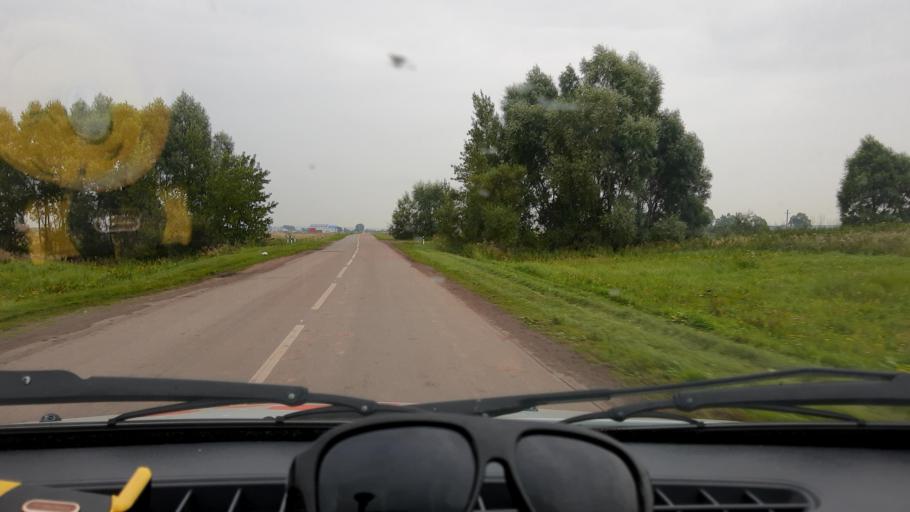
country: RU
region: Bashkortostan
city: Blagoveshchensk
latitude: 55.0036
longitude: 55.7379
